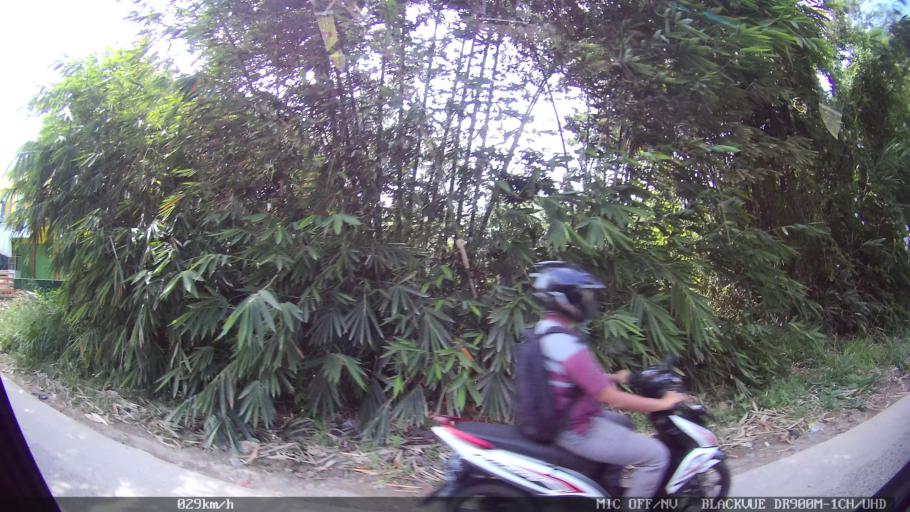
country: ID
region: Lampung
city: Kedaton
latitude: -5.3408
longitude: 105.2726
